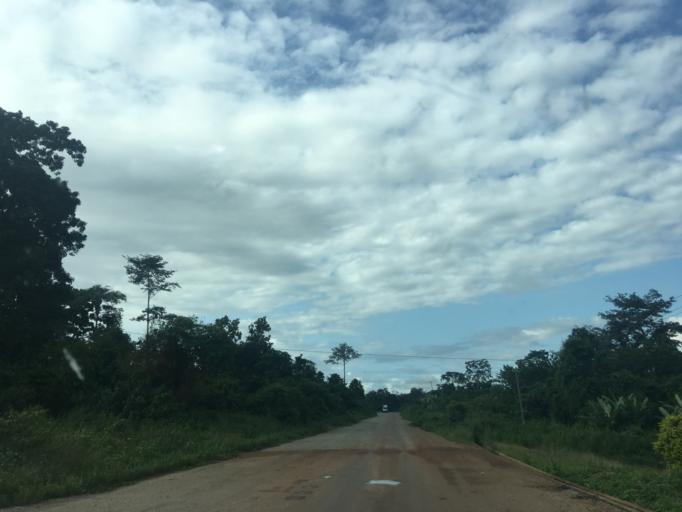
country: GH
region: Western
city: Wassa-Akropong
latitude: 6.0087
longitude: -2.4064
